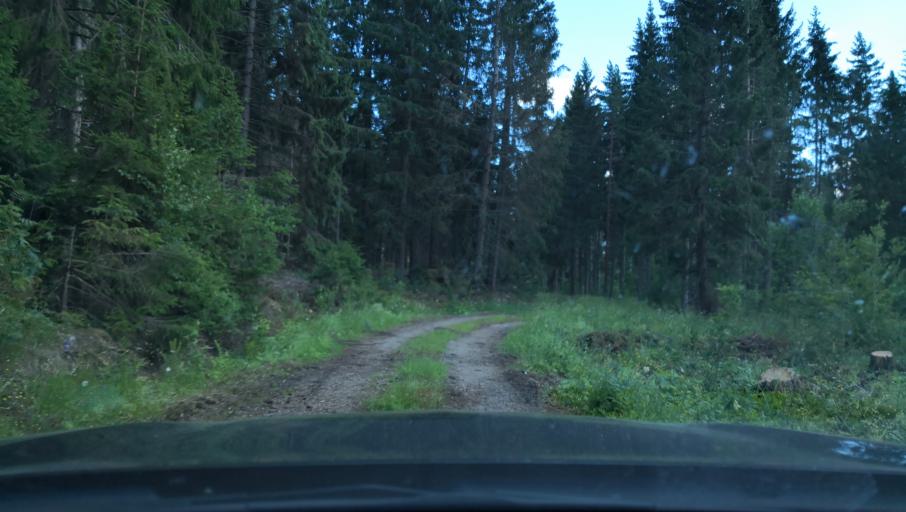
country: SE
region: Vaestmanland
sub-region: Kungsors Kommun
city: Kungsoer
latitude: 59.3393
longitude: 16.0630
